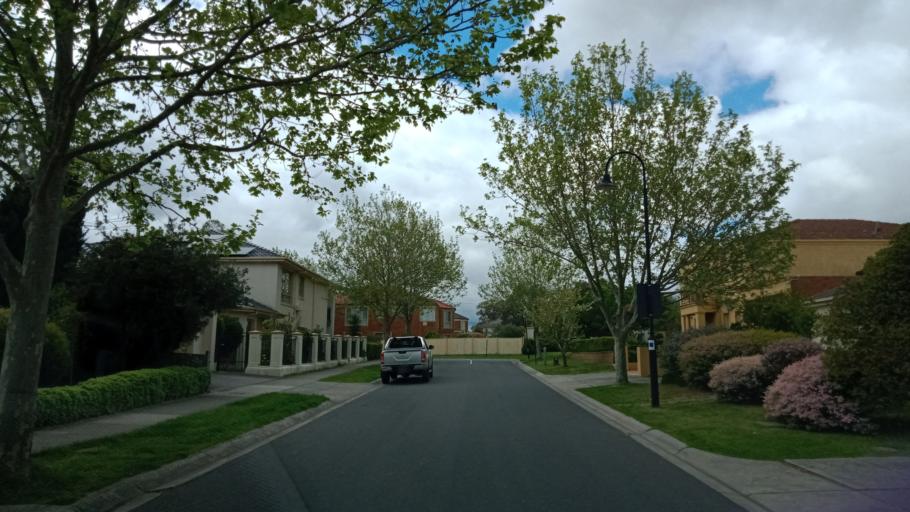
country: AU
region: Victoria
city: Burwood East
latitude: -37.8665
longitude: 145.1601
